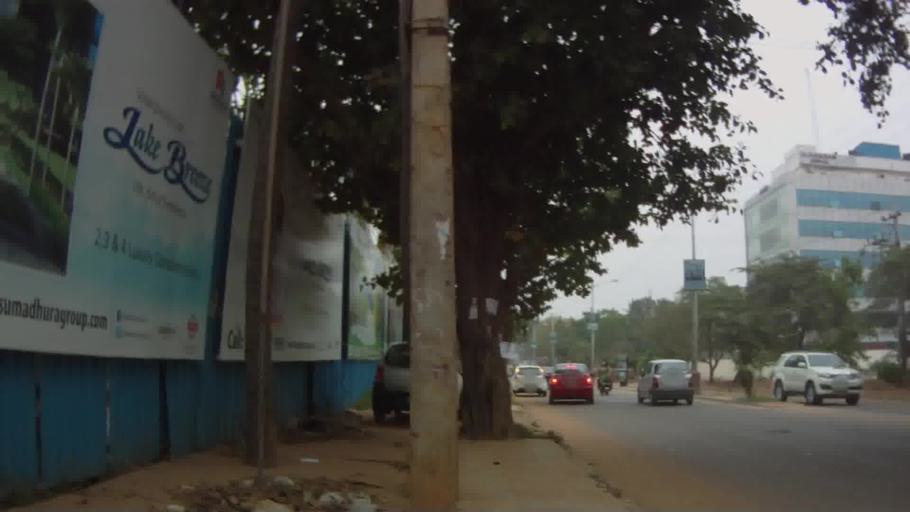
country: IN
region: Karnataka
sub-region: Bangalore Urban
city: Bangalore
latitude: 12.9559
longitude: 77.7242
